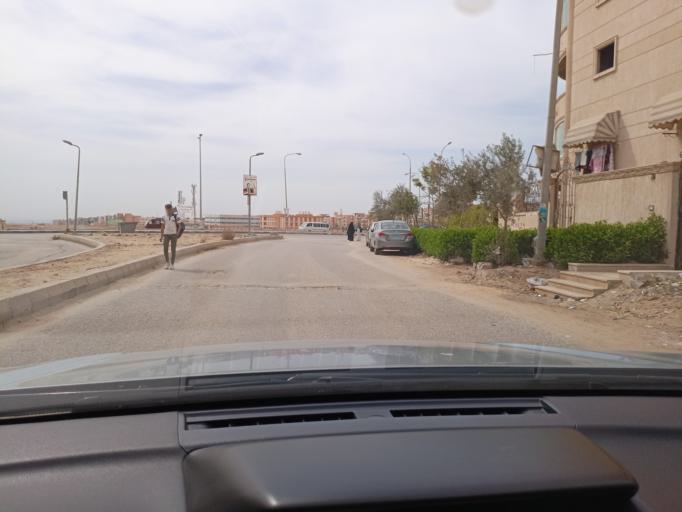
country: EG
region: Muhafazat al Qalyubiyah
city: Al Khankah
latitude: 30.2408
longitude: 31.4824
